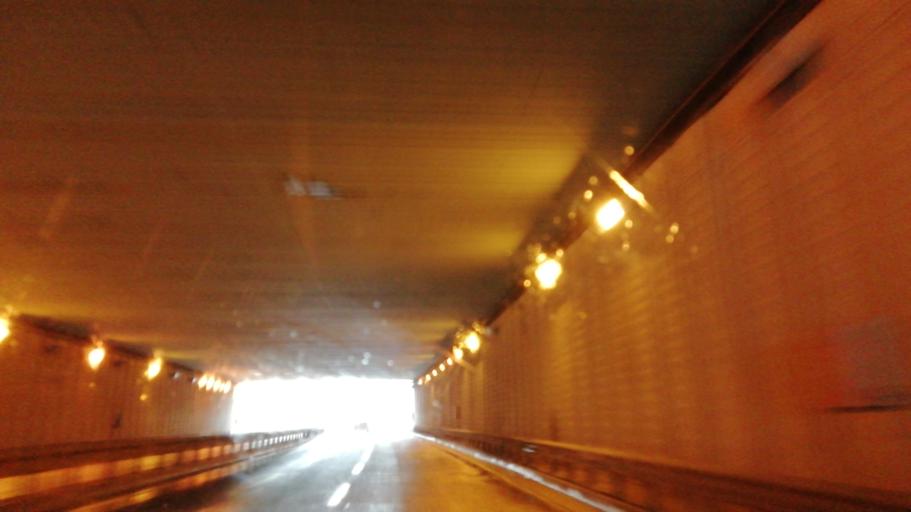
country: TR
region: Istanbul
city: Yakuplu
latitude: 40.9885
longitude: 28.7215
